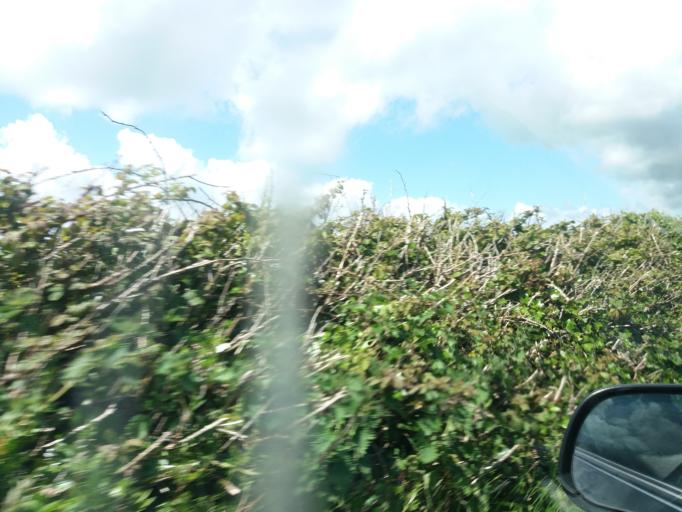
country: IE
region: Munster
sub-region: Waterford
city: Dunmore East
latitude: 52.1776
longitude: -6.8945
